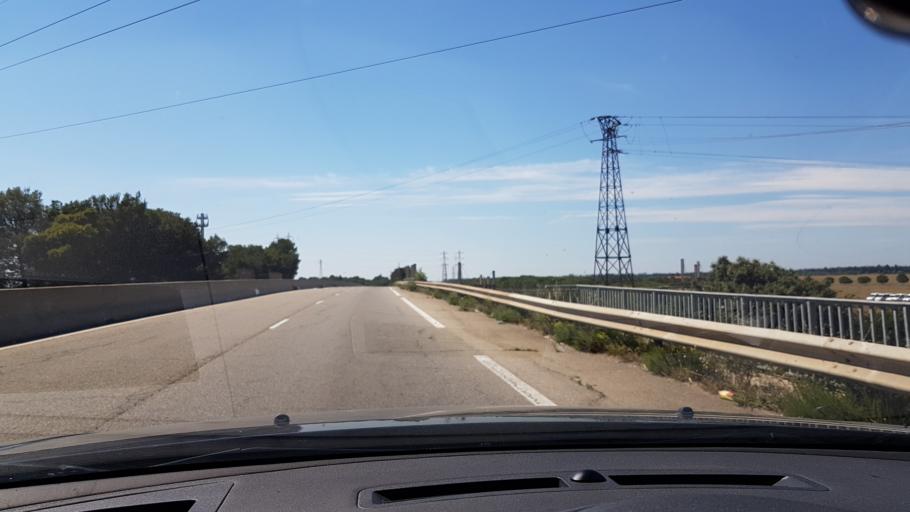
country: FR
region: Provence-Alpes-Cote d'Azur
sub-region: Departement des Bouches-du-Rhone
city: Fos-sur-Mer
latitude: 43.4736
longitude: 4.9036
